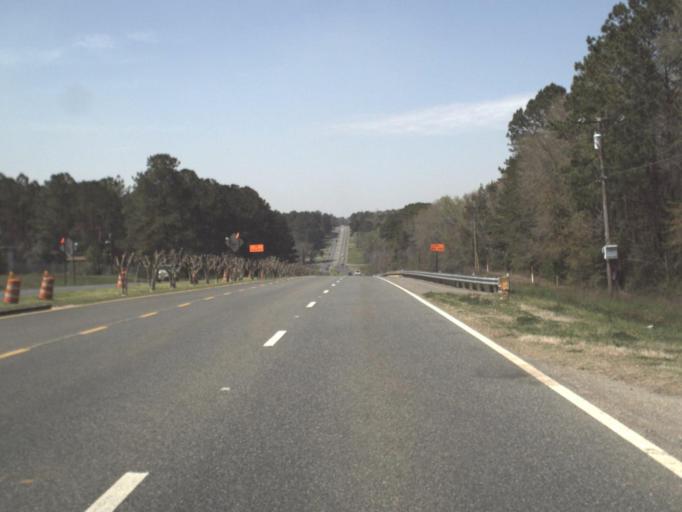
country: US
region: Florida
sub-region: Gadsden County
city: Quincy
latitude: 30.5742
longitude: -84.5530
